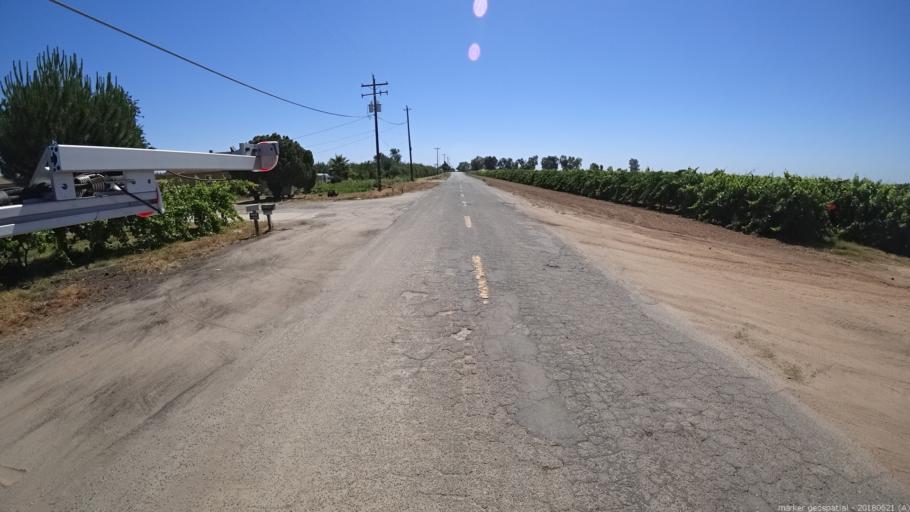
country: US
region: California
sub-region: Madera County
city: Parksdale
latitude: 36.9094
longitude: -119.9652
